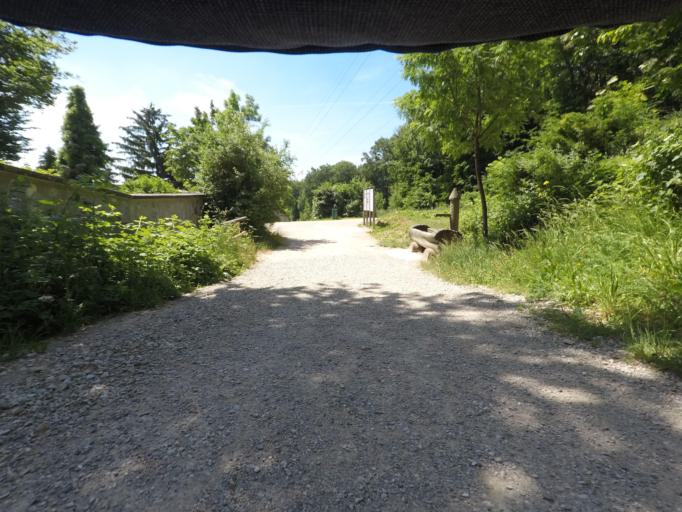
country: AT
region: Lower Austria
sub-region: Politischer Bezirk Modling
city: Perchtoldsdorf
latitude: 48.1771
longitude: 16.2528
